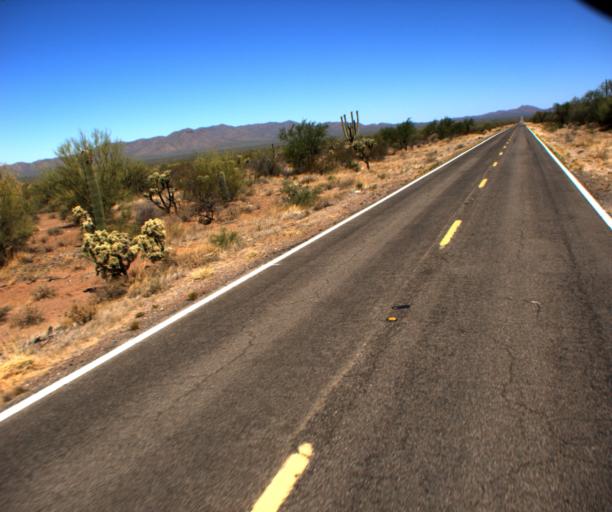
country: US
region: Arizona
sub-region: Pima County
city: Sells
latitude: 32.0670
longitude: -112.0389
